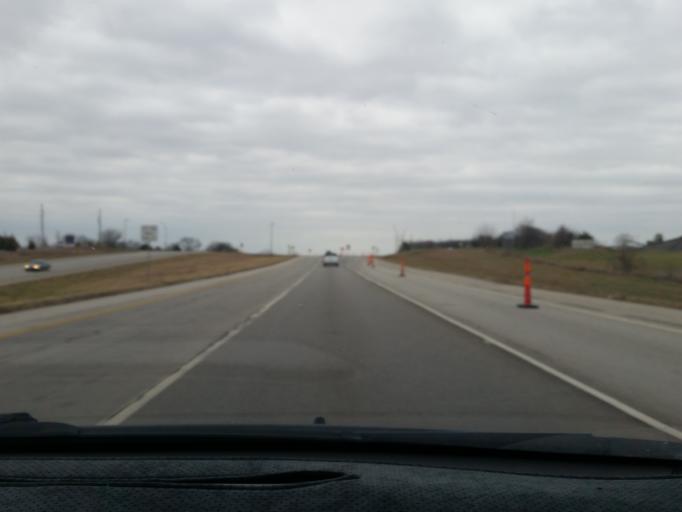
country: US
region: Kansas
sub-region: Douglas County
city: Lawrence
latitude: 38.9423
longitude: -95.1899
